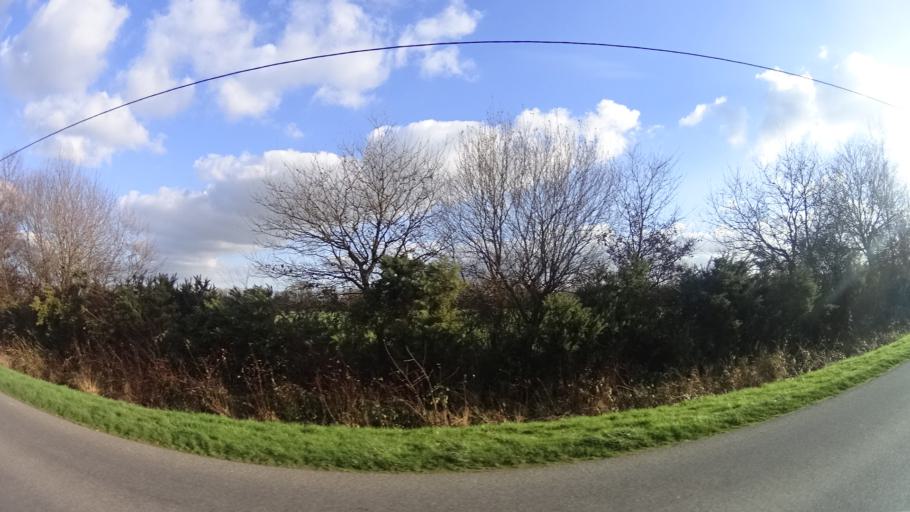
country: FR
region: Pays de la Loire
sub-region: Departement de la Loire-Atlantique
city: Guemene-Penfao
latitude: 47.5944
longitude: -1.8502
